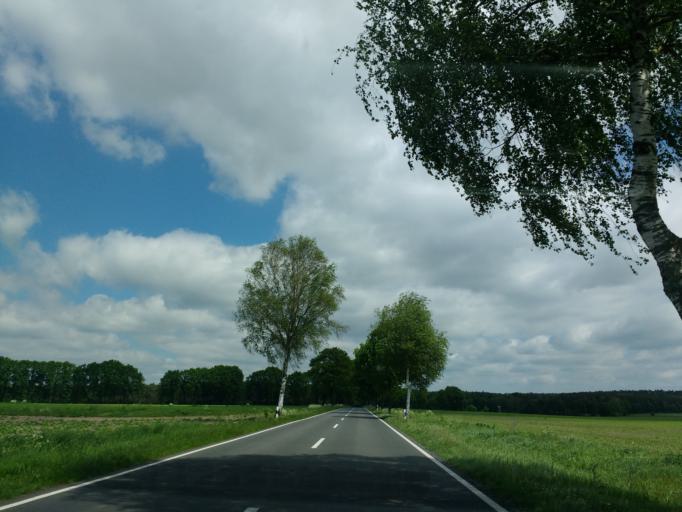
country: DE
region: Lower Saxony
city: Bad Fallingbostel
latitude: 52.8410
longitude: 9.6464
